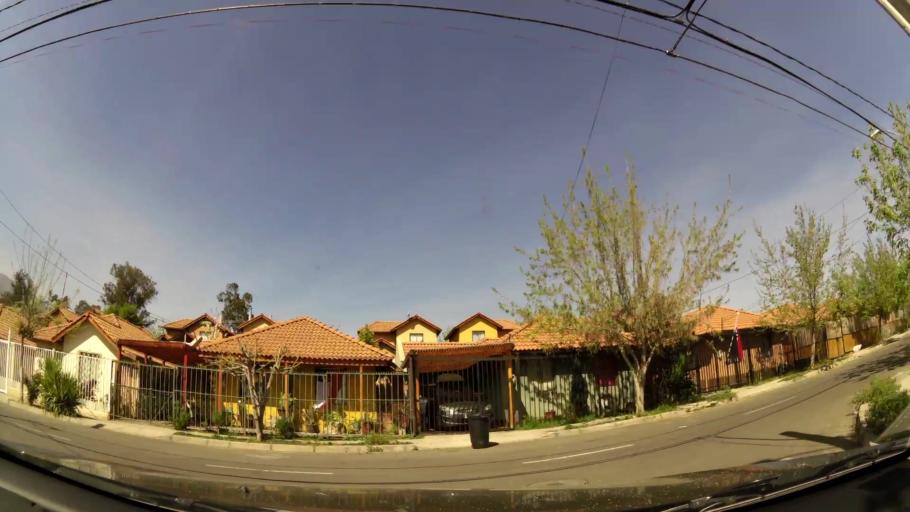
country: CL
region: Santiago Metropolitan
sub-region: Provincia de Cordillera
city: Puente Alto
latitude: -33.5907
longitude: -70.5369
